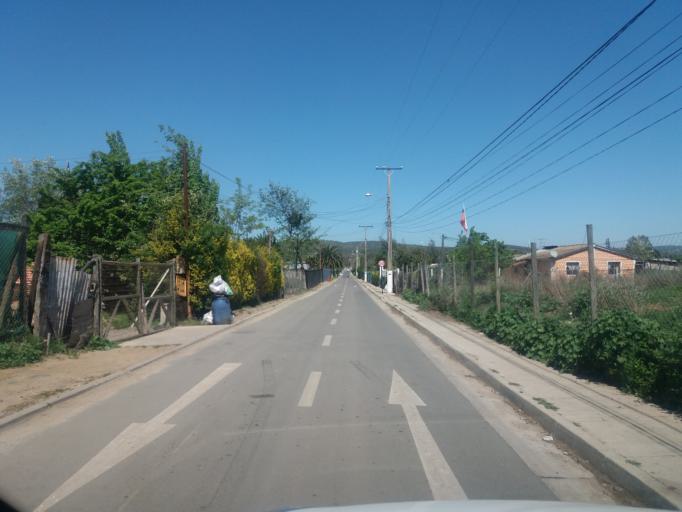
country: CL
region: Valparaiso
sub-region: Provincia de Marga Marga
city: Limache
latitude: -32.9787
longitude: -71.2878
